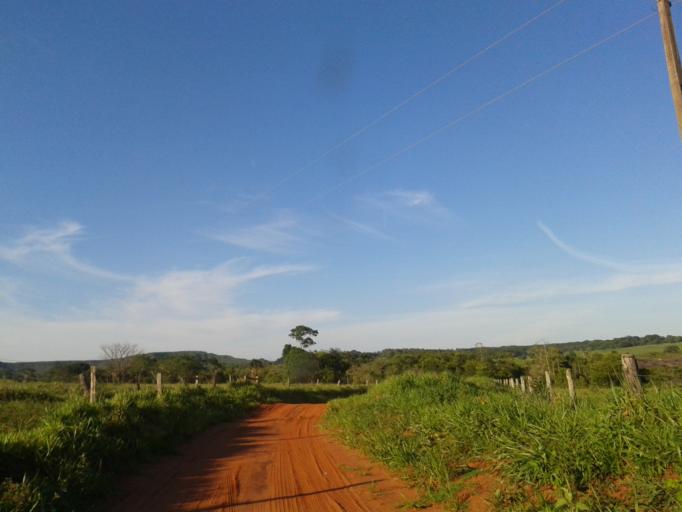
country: BR
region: Minas Gerais
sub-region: Santa Vitoria
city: Santa Vitoria
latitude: -18.9610
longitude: -49.8667
